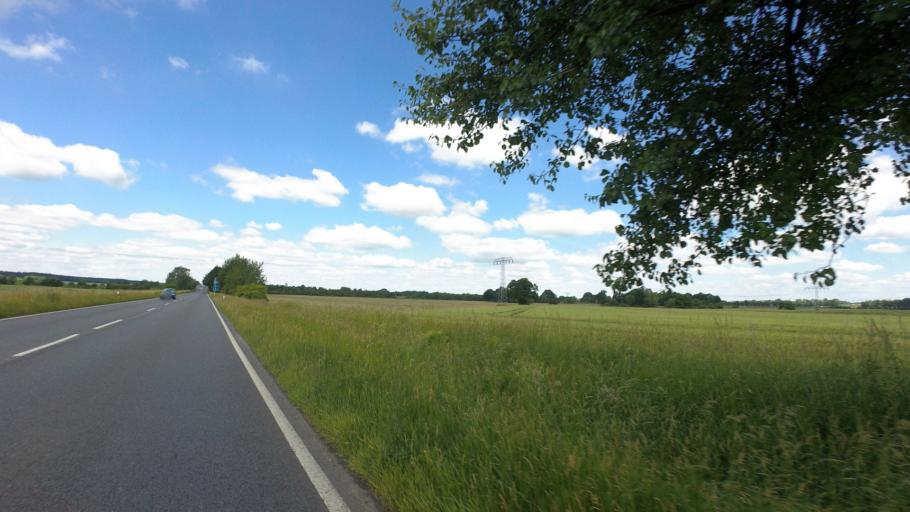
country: DE
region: Brandenburg
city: Grossraschen
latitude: 51.5859
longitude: 13.9505
